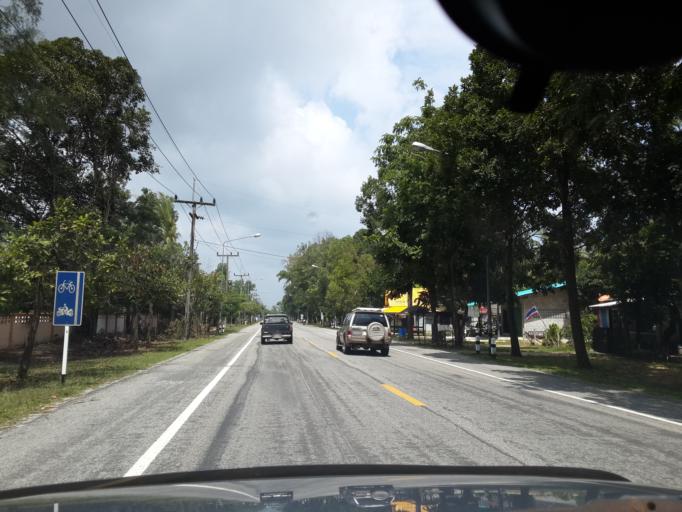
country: TH
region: Narathiwat
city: Bacho
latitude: 6.5172
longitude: 101.7545
